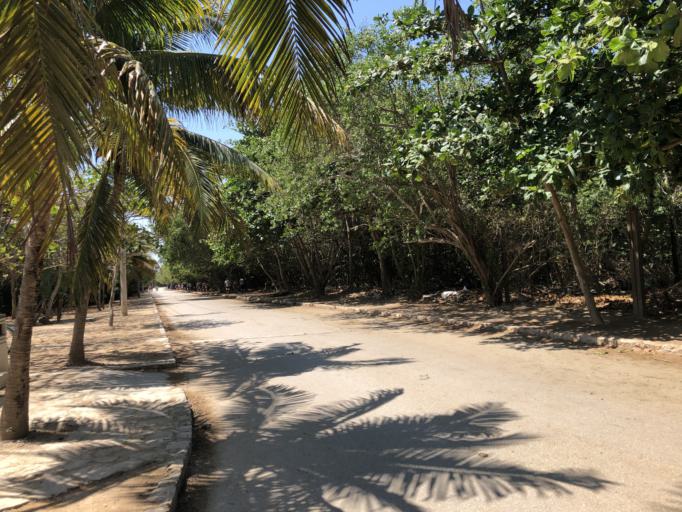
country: MX
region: Quintana Roo
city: Tulum
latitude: 20.2149
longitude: -87.4309
